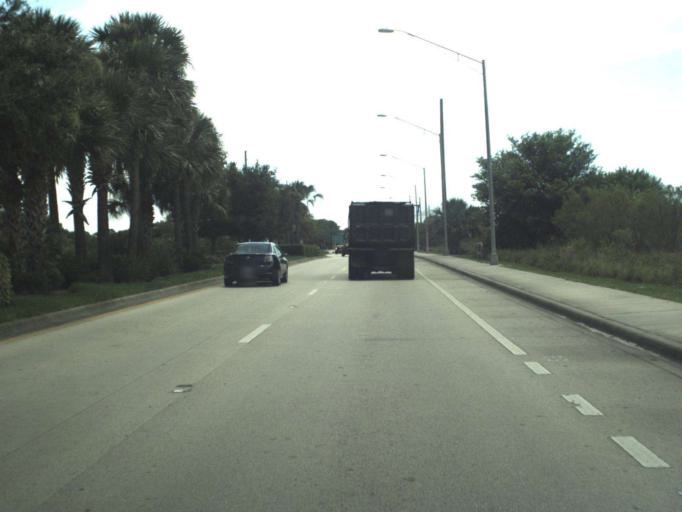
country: US
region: Florida
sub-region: Indian River County
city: Vero Beach South
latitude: 27.6121
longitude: -80.3858
